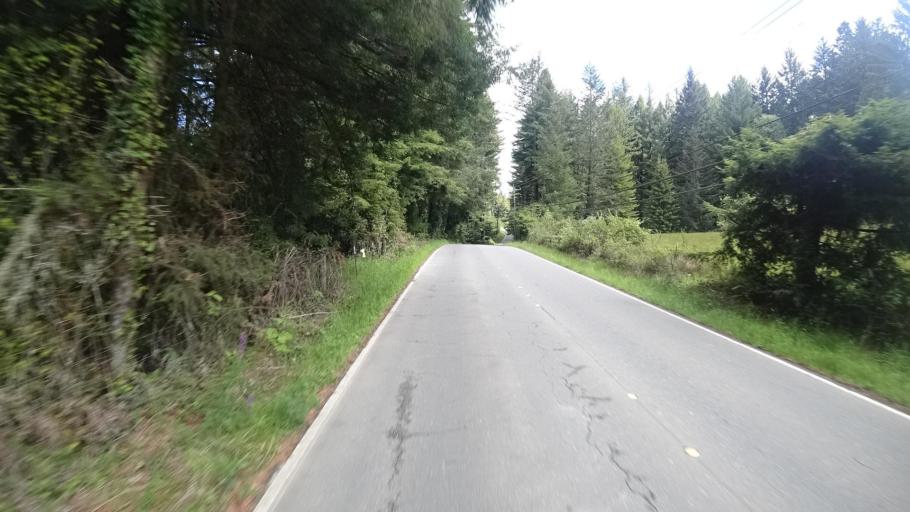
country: US
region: California
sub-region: Humboldt County
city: Blue Lake
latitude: 40.9178
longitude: -124.0225
